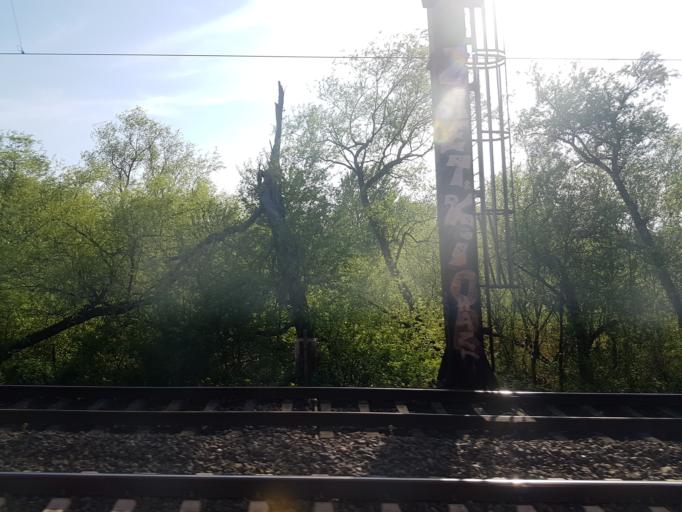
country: DE
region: Lower Saxony
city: Hannover
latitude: 52.3456
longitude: 9.7420
